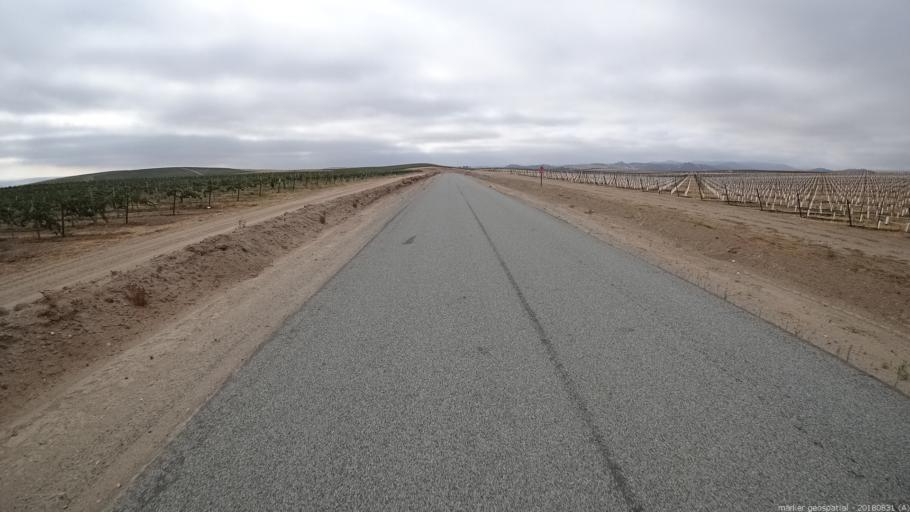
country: US
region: California
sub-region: Monterey County
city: King City
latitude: 36.1681
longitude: -121.1168
